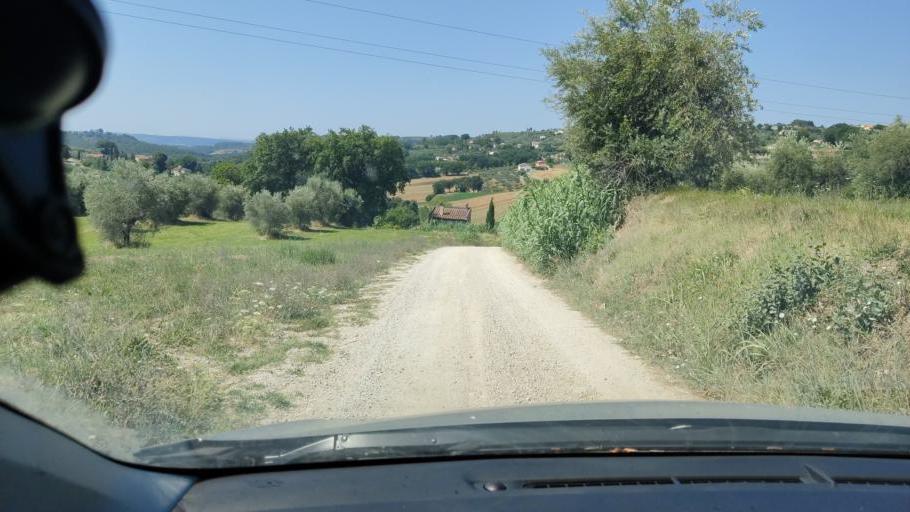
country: IT
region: Umbria
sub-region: Provincia di Terni
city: Amelia
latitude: 42.5454
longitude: 12.4298
